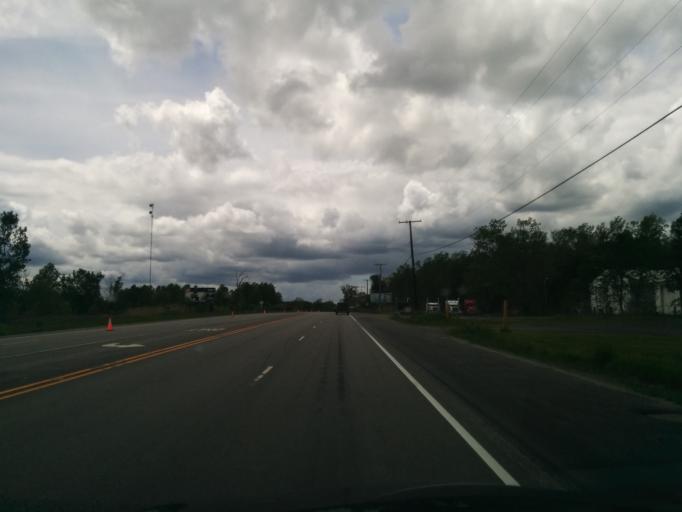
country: US
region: Indiana
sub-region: Porter County
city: Chesterton
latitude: 41.6369
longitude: -87.0487
